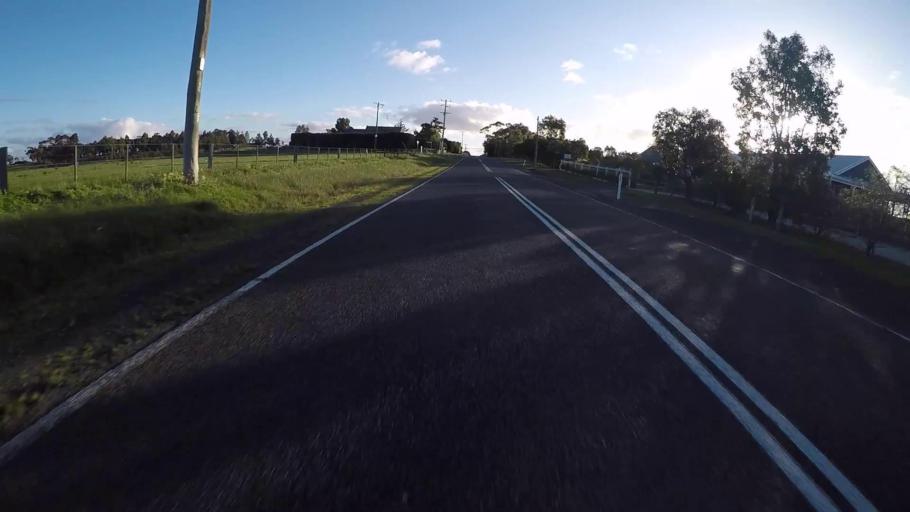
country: AU
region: Victoria
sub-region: Greater Geelong
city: Wandana Heights
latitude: -38.1693
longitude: 144.2117
